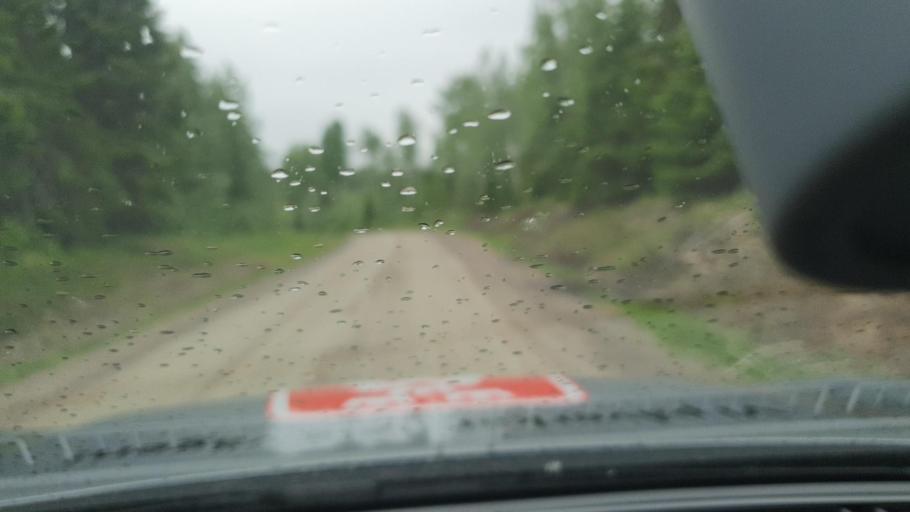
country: SE
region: Norrbotten
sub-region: Kalix Kommun
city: Rolfs
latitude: 66.0754
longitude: 22.9730
